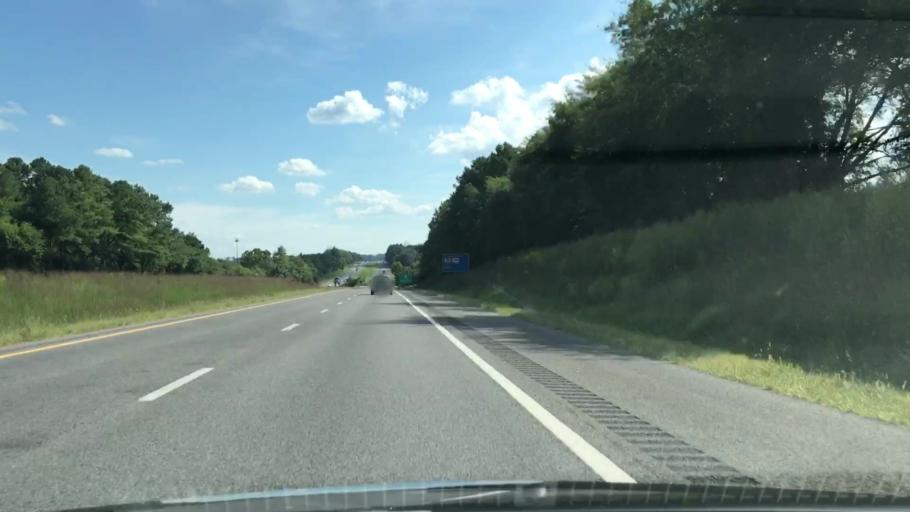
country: US
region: Tennessee
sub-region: Marshall County
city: Cornersville
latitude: 35.3222
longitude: -86.8822
